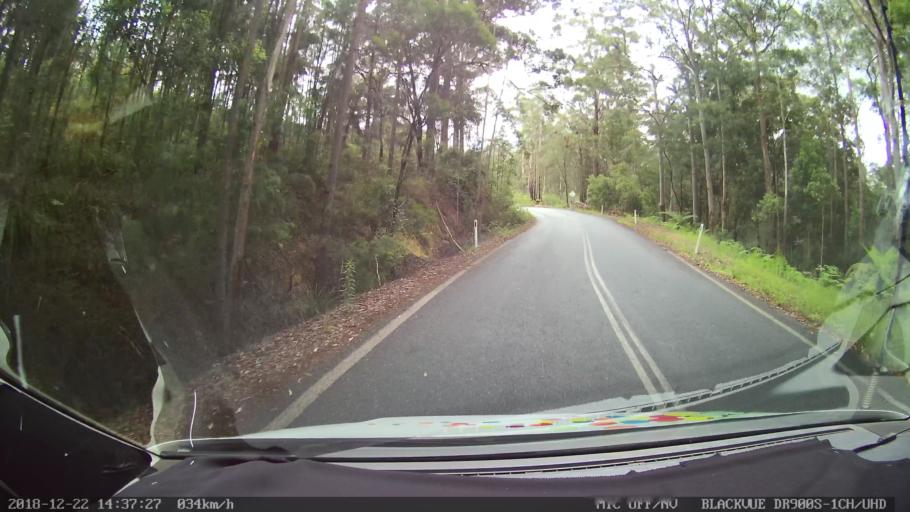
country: AU
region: New South Wales
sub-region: Bellingen
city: Dorrigo
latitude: -30.1329
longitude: 152.6018
